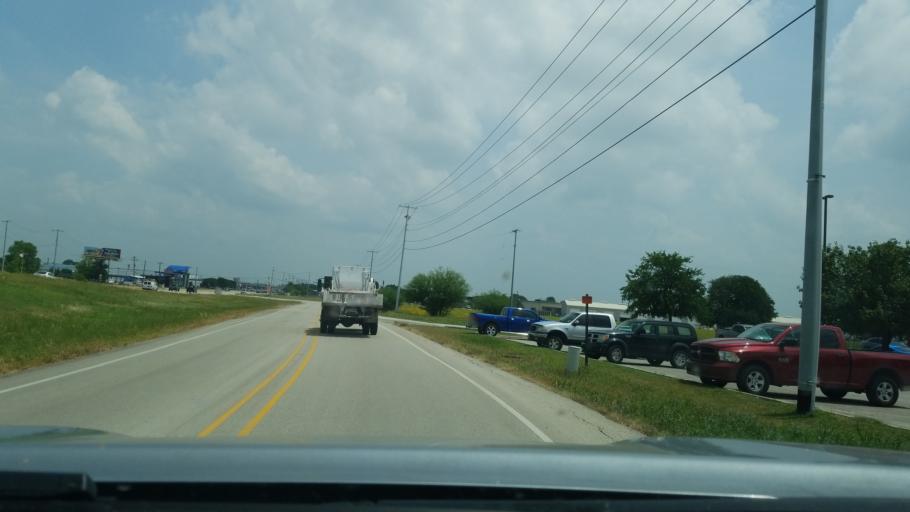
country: US
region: Texas
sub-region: Comal County
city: New Braunfels
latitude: 29.7359
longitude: -98.0871
